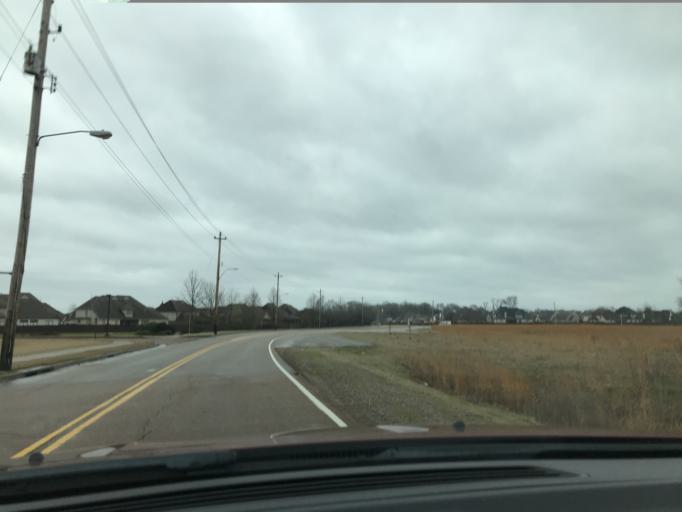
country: US
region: Tennessee
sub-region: Shelby County
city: Collierville
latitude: 35.0899
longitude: -89.7084
